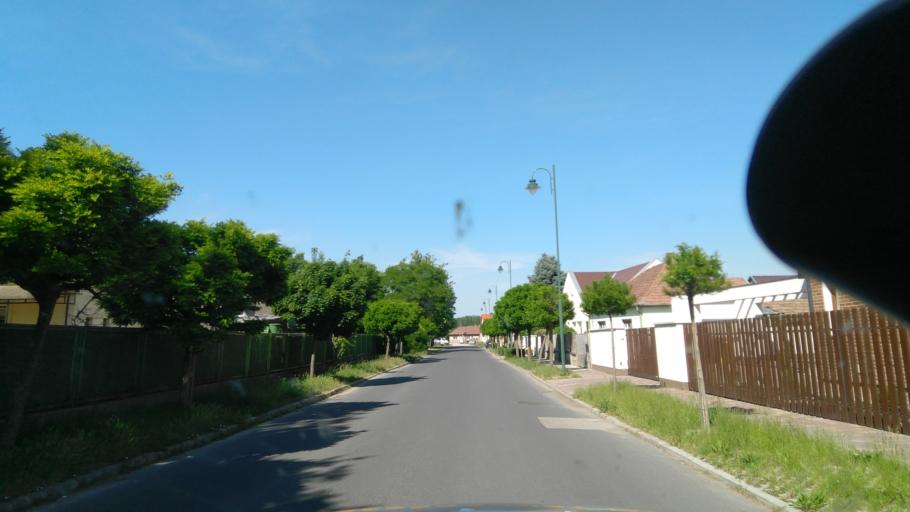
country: HU
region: Bekes
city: Gyula
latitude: 46.6444
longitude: 21.2890
